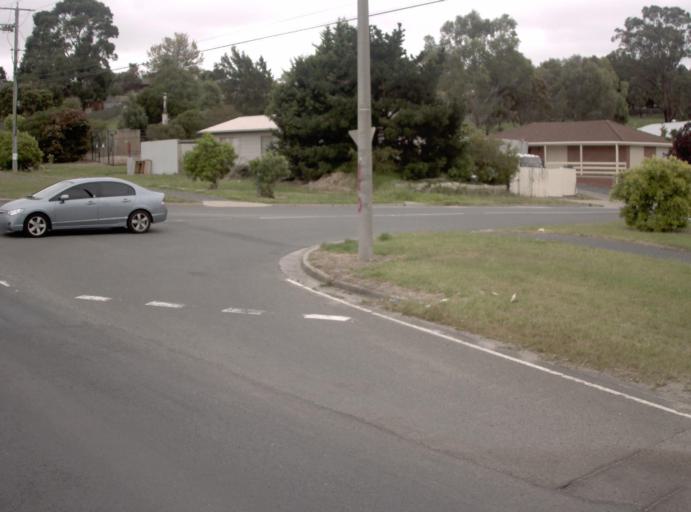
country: AU
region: Victoria
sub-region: Casey
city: Hallam
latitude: -38.0238
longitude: 145.2697
